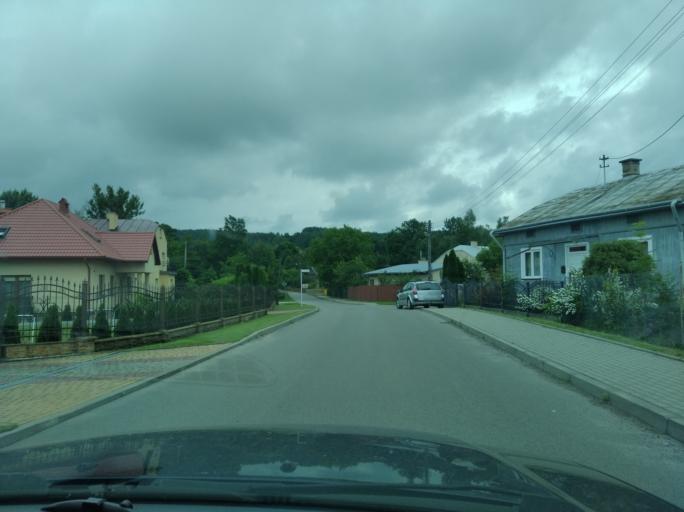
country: PL
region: Subcarpathian Voivodeship
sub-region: Powiat jaroslawski
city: Pruchnik
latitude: 49.9027
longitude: 22.5137
